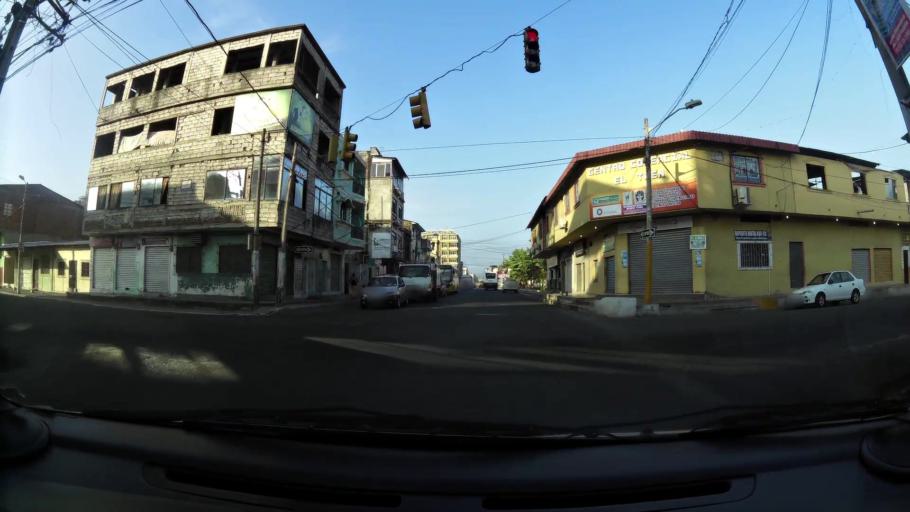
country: EC
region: Guayas
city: Eloy Alfaro
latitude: -2.1689
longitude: -79.8519
